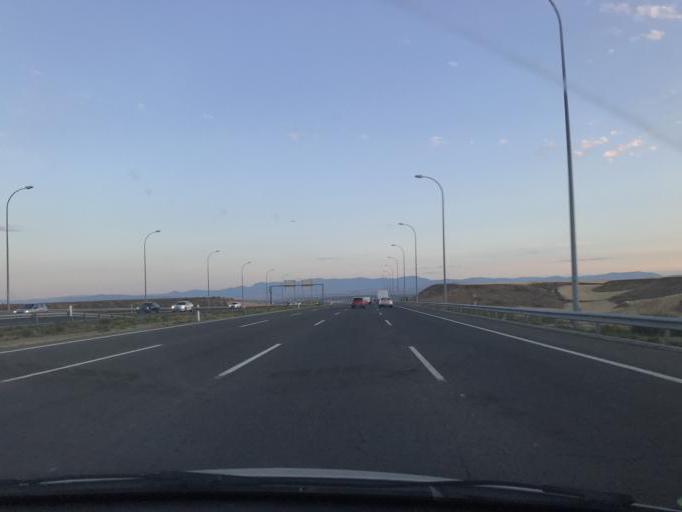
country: ES
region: Madrid
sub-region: Provincia de Madrid
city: Paracuellos de Jarama
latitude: 40.5288
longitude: -3.5167
